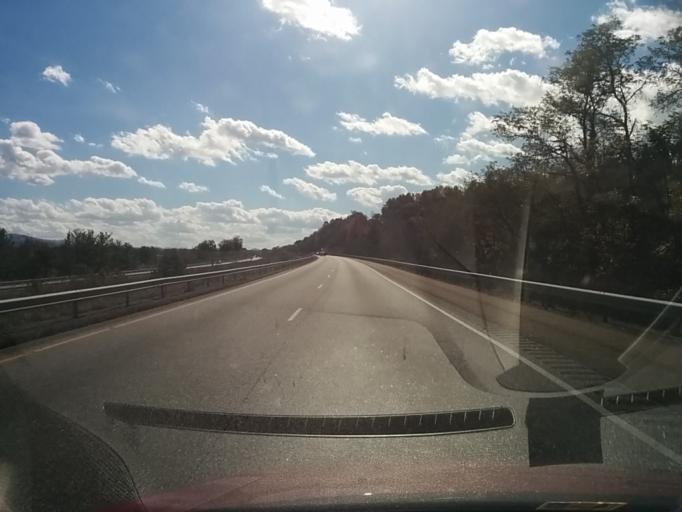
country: US
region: Virginia
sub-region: Augusta County
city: Stuarts Draft
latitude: 38.0014
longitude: -79.1738
